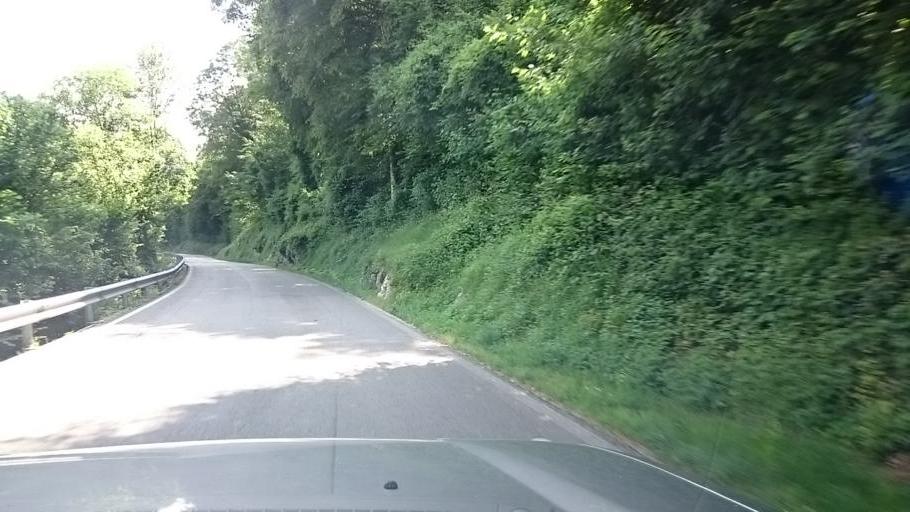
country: IT
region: Veneto
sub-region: Provincia di Vicenza
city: Conco
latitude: 45.7868
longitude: 11.6047
